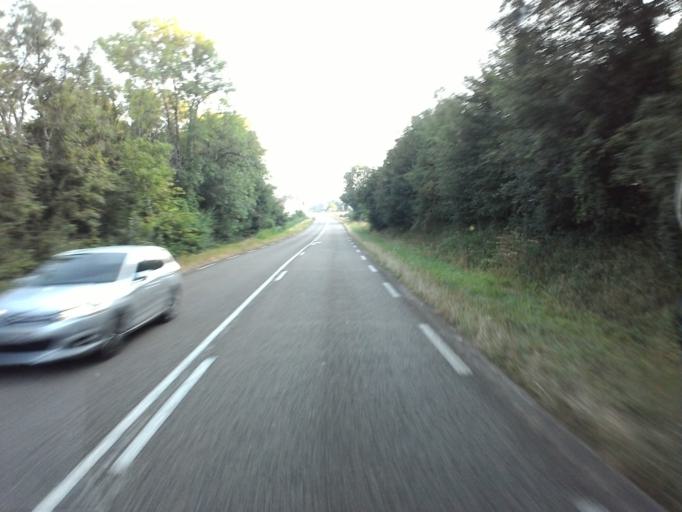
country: FR
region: Franche-Comte
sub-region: Departement de la Haute-Saone
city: Echenoz-la-Meline
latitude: 47.5858
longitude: 6.1378
